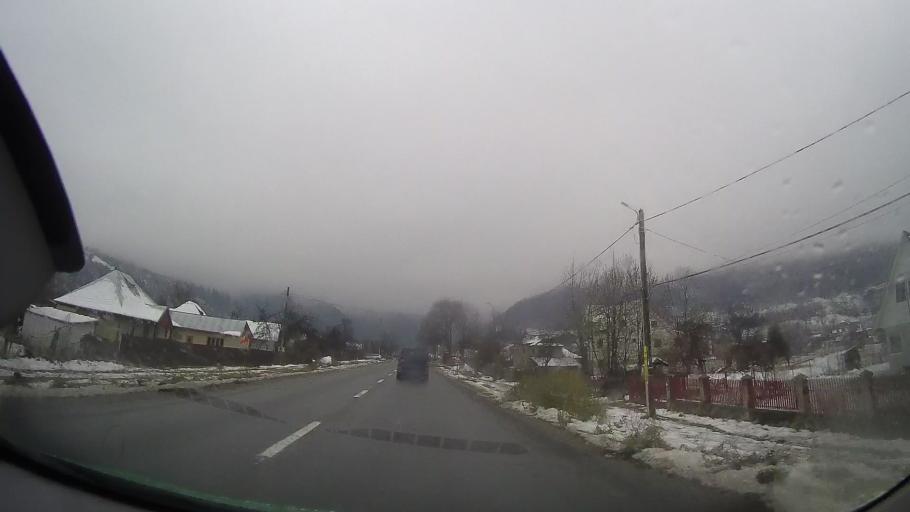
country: RO
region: Neamt
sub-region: Comuna Pangarati
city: Stejaru
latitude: 46.9025
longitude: 26.1741
